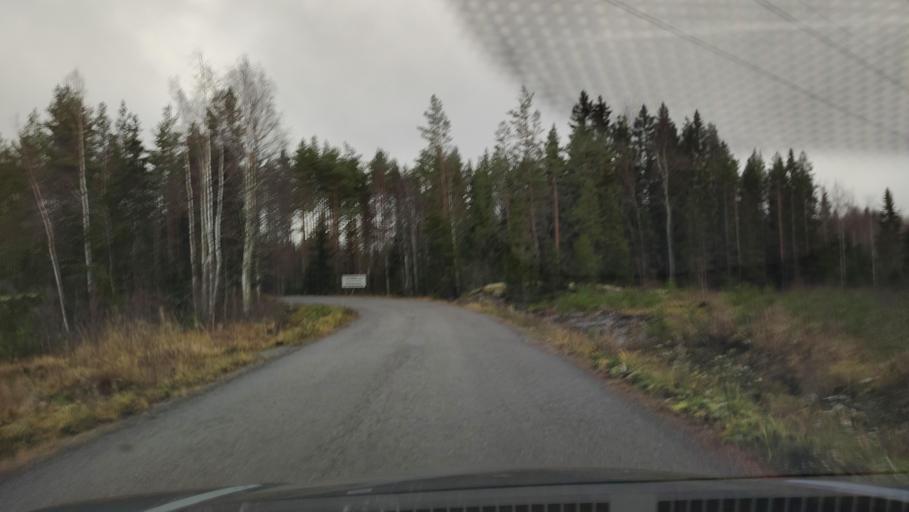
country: FI
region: Ostrobothnia
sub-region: Sydosterbotten
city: Kristinestad
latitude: 62.1486
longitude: 21.5532
